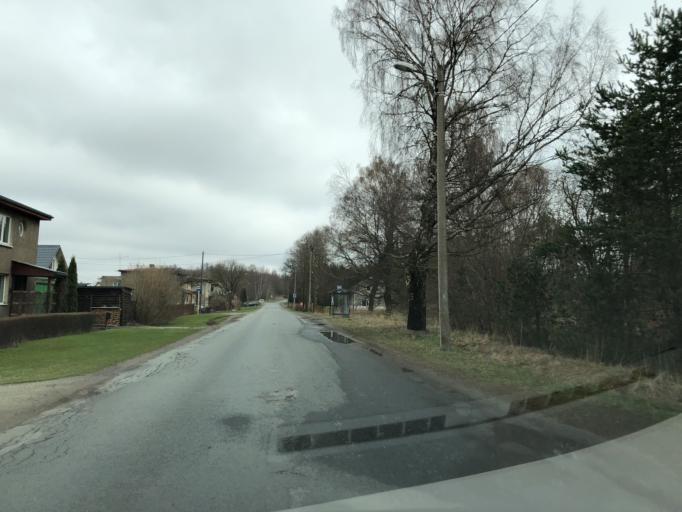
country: EE
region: Laeaene-Virumaa
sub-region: Rakvere linn
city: Rakvere
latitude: 59.3288
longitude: 26.3498
